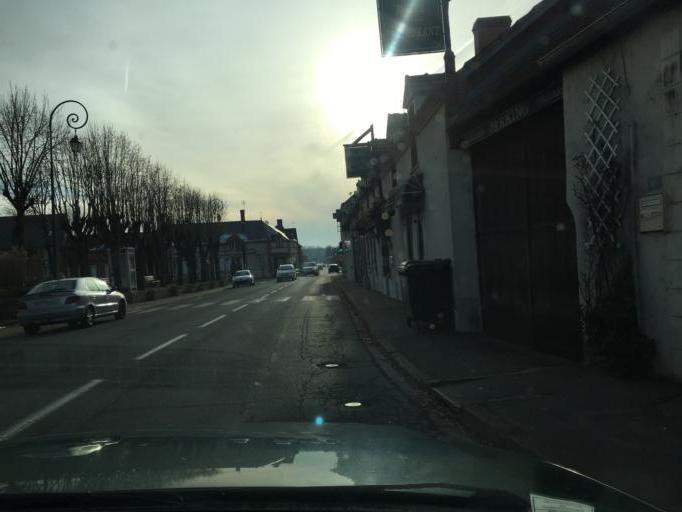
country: FR
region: Centre
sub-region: Departement du Loiret
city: Marcilly-en-Villette
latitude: 47.7651
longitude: 2.0215
